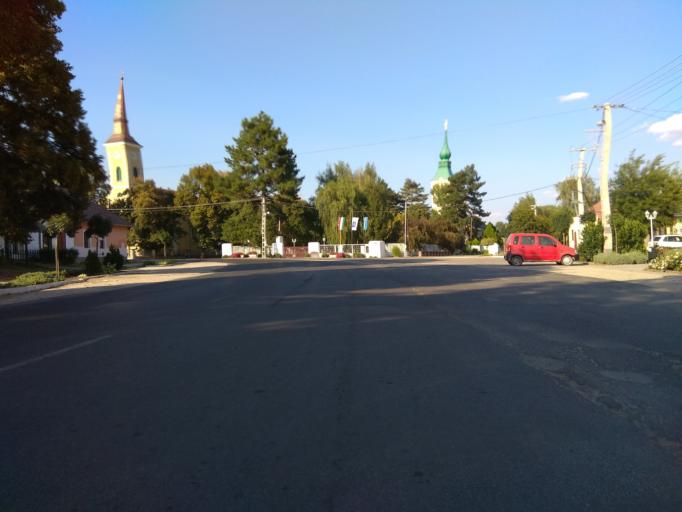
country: HU
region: Borsod-Abauj-Zemplen
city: Onod
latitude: 48.0024
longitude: 20.9177
